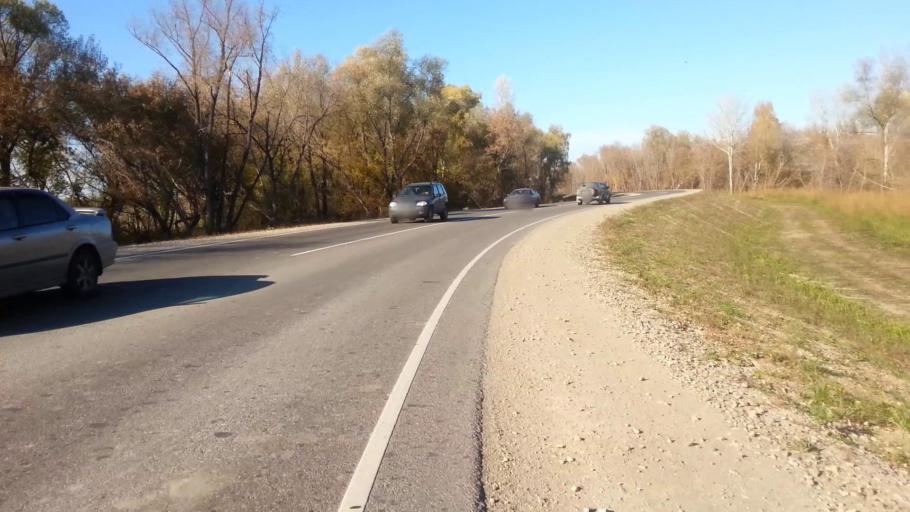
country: RU
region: Altai Krai
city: Sannikovo
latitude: 53.3220
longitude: 83.9427
